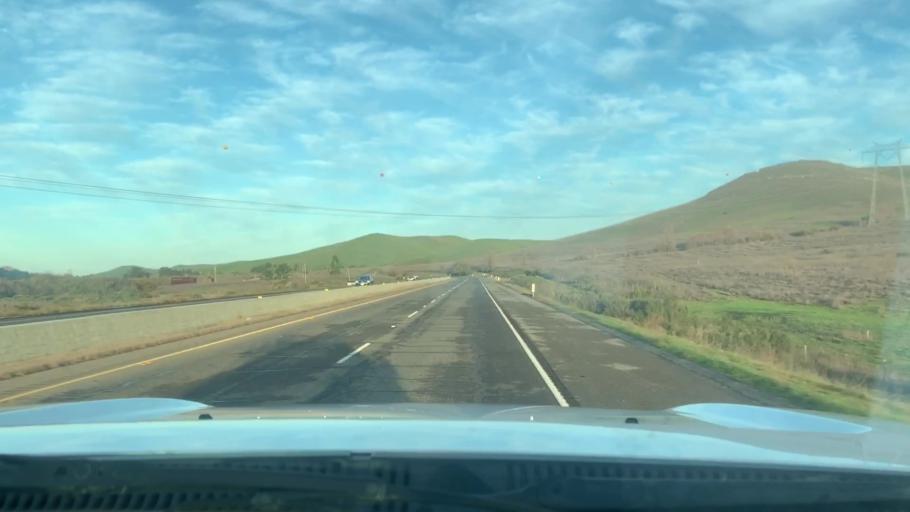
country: US
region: California
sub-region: San Luis Obispo County
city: Los Osos
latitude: 35.3494
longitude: -120.7722
